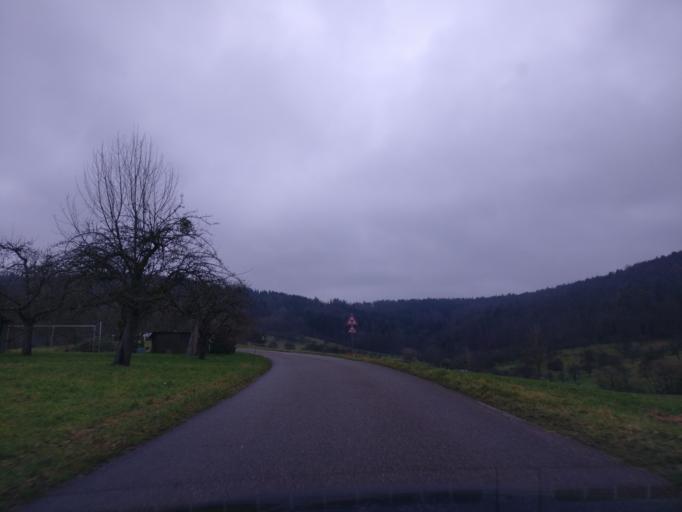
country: DE
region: Baden-Wuerttemberg
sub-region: Regierungsbezirk Stuttgart
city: Rudersberg
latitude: 48.8745
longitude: 9.5081
